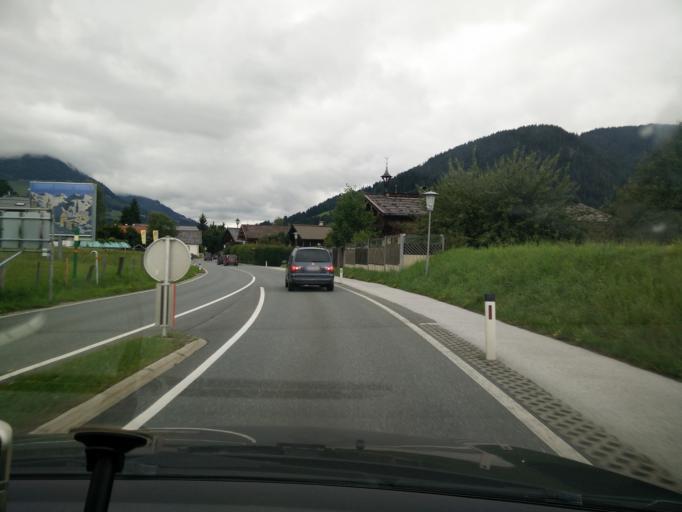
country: AT
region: Tyrol
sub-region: Politischer Bezirk Kitzbuhel
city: Reith bei Kitzbuhel
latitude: 47.4562
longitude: 12.3549
